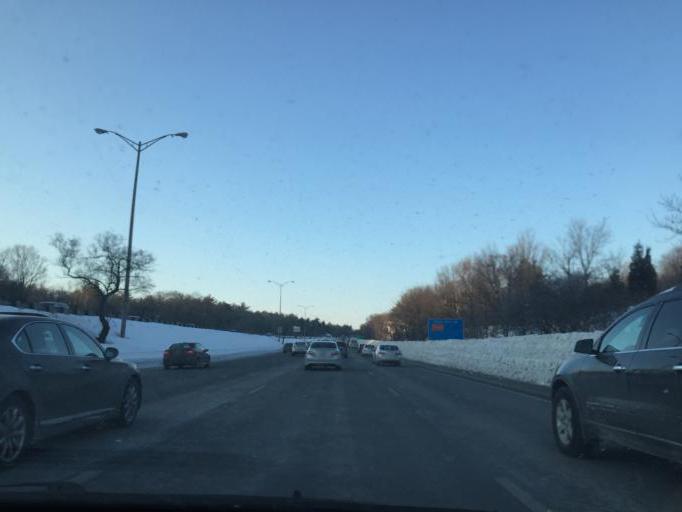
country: US
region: Massachusetts
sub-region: Middlesex County
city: Medford
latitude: 42.4386
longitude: -71.1035
